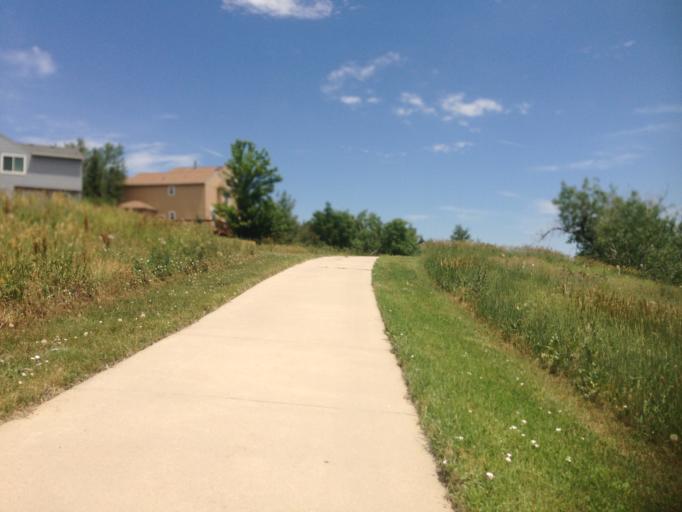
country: US
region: Colorado
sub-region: Boulder County
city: Superior
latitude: 39.9299
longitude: -105.1630
